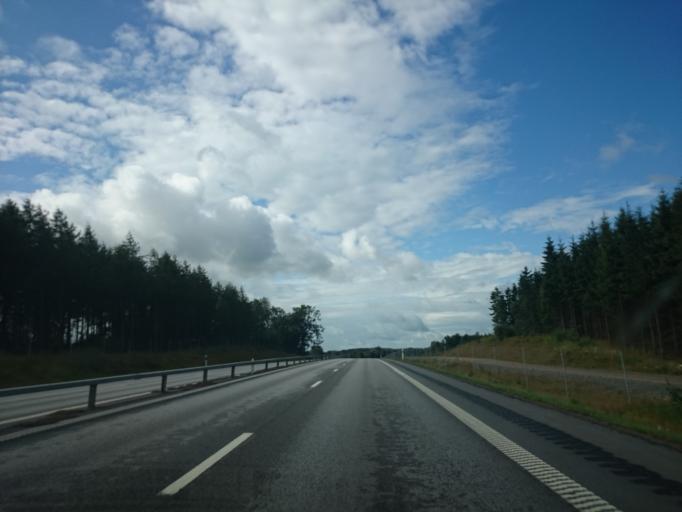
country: SE
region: Skane
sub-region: Horby Kommun
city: Hoerby
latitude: 55.8799
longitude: 13.7127
